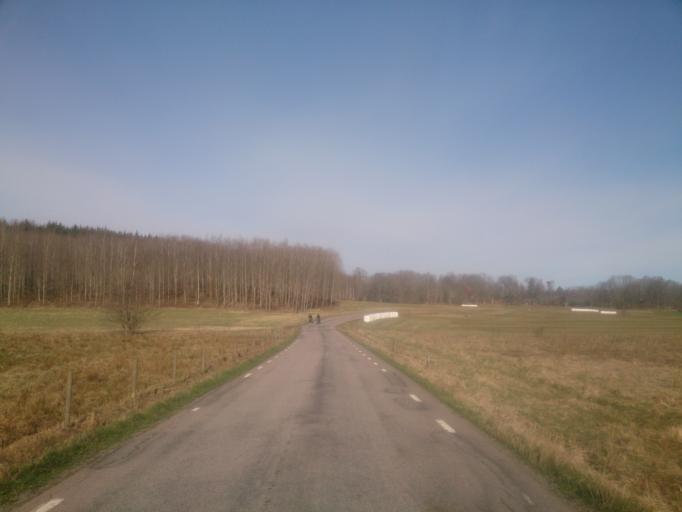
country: SE
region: OEstergoetland
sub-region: Linkopings Kommun
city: Sturefors
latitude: 58.2945
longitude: 15.8529
